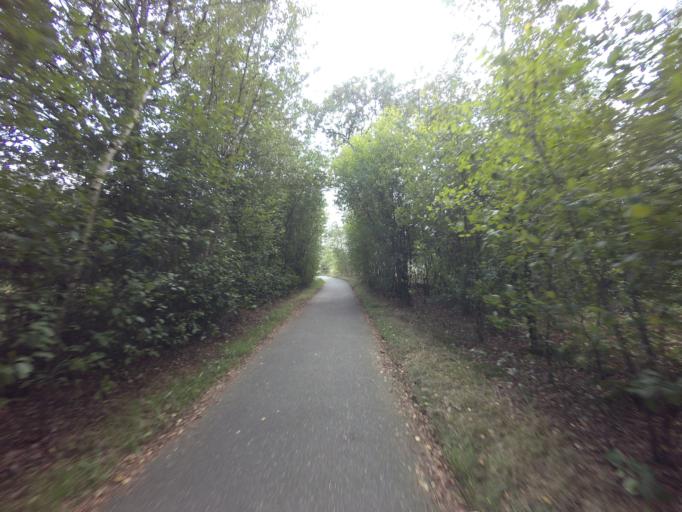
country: NL
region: Drenthe
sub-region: Gemeente Westerveld
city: Dwingeloo
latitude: 52.8340
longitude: 6.4690
